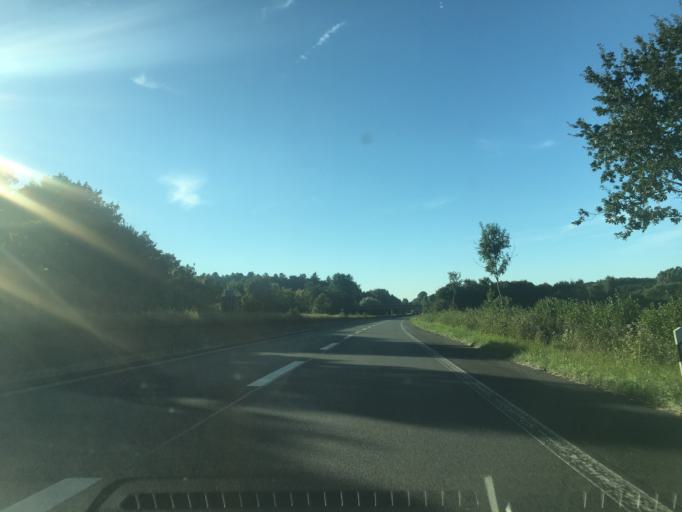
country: DE
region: North Rhine-Westphalia
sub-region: Regierungsbezirk Munster
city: Dulmen
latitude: 51.8472
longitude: 7.2915
